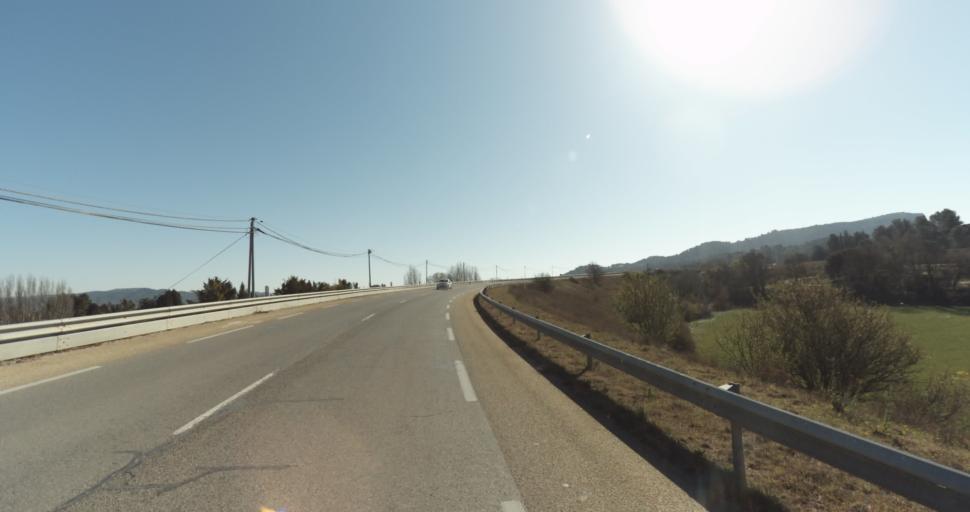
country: FR
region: Provence-Alpes-Cote d'Azur
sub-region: Departement des Bouches-du-Rhone
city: Meyrargues
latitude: 43.6442
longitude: 5.5200
